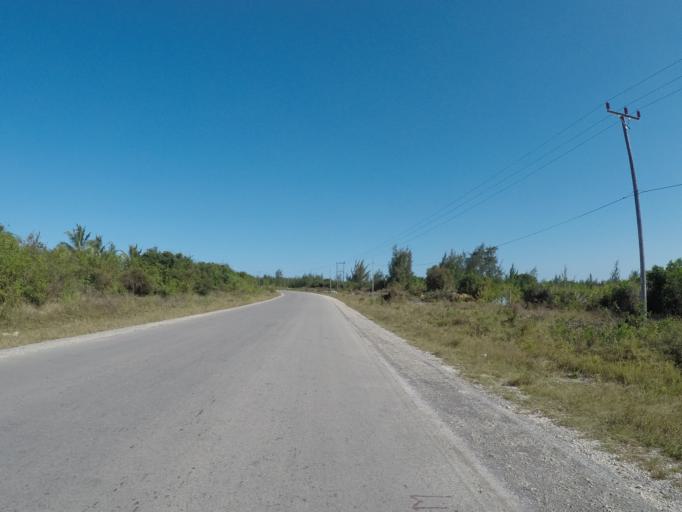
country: TZ
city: Kiwengwa
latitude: -6.1602
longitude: 39.5201
